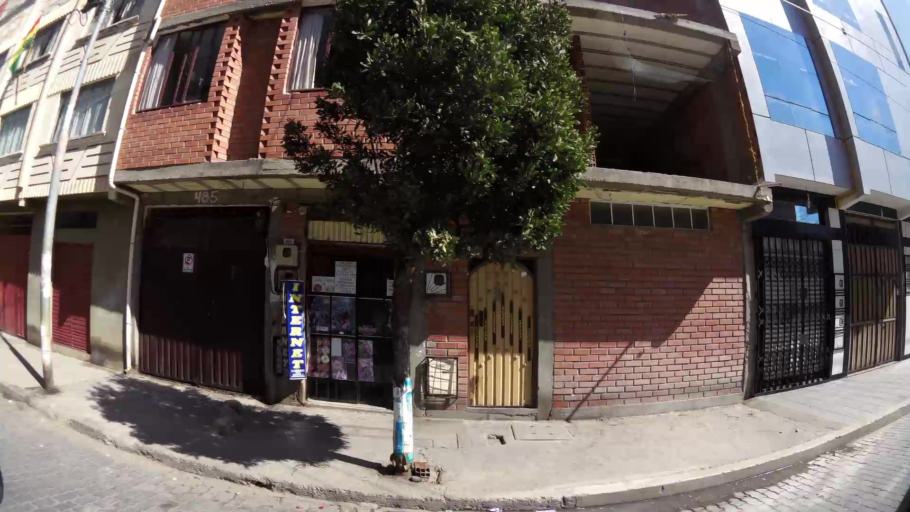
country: BO
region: La Paz
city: La Paz
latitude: -16.5203
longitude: -68.1560
